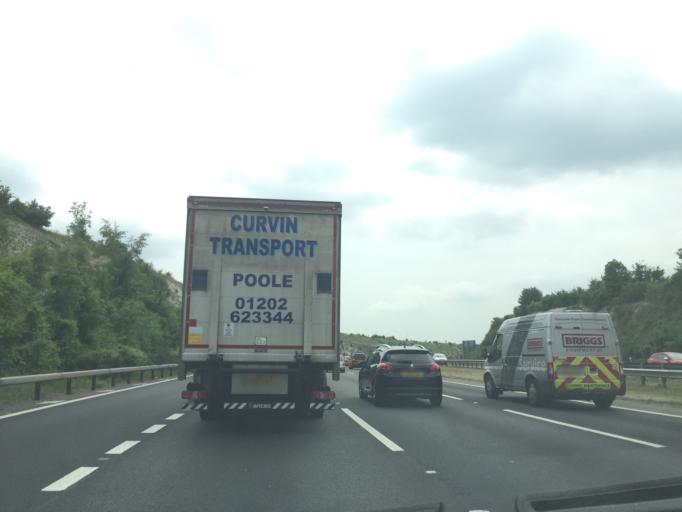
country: GB
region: England
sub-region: Hampshire
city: Winchester
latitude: 51.0461
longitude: -1.3031
